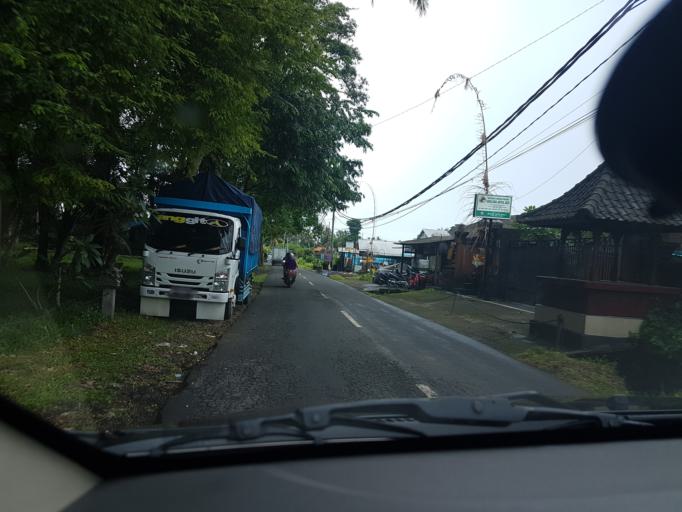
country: ID
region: Bali
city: Banjar Pande
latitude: -8.5205
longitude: 115.2394
